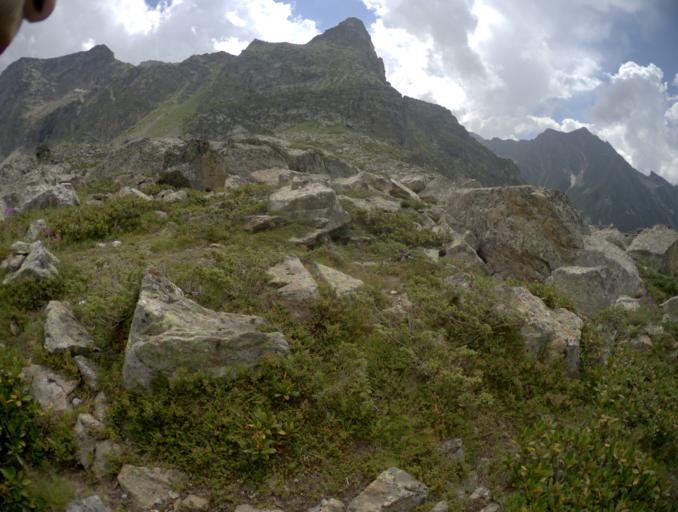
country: RU
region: Karachayevo-Cherkesiya
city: Uchkulan
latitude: 43.2896
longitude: 42.0806
